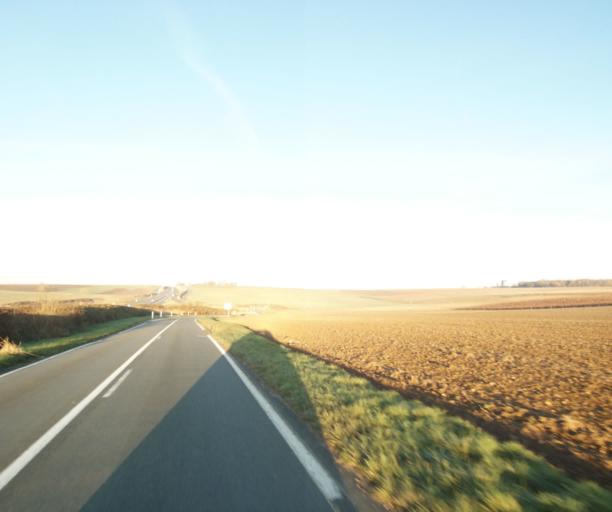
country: FR
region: Poitou-Charentes
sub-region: Departement de la Charente-Maritime
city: Cherac
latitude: 45.7055
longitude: -0.4769
